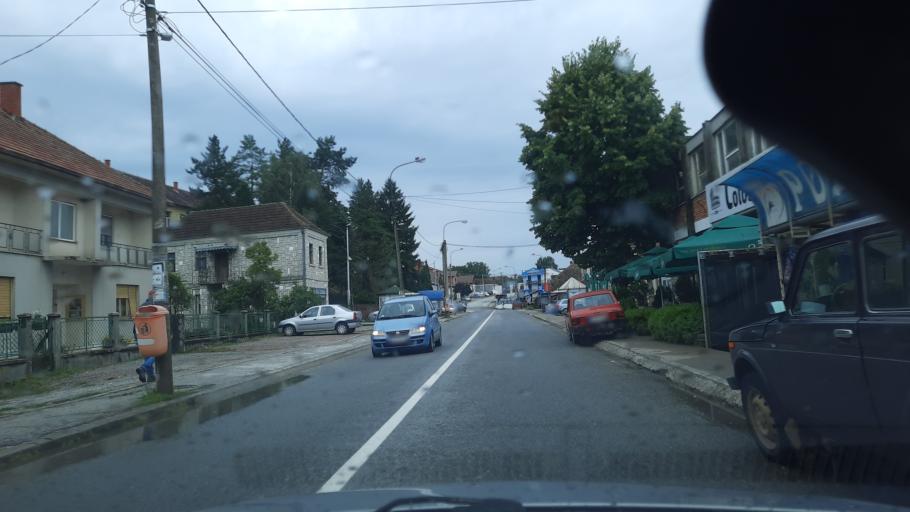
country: RS
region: Central Serbia
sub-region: Sumadijski Okrug
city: Knic
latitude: 43.8966
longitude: 20.7712
